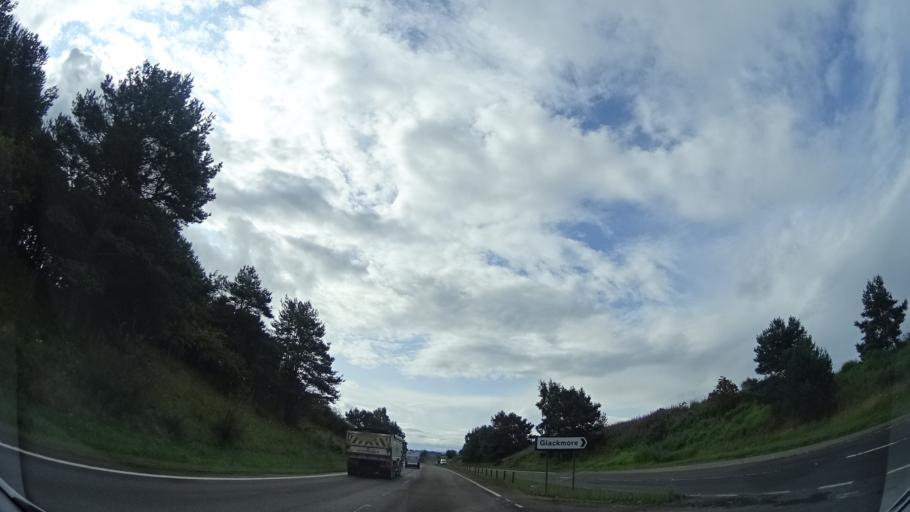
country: GB
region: Scotland
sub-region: Highland
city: Inverness
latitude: 57.5307
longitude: -4.3267
